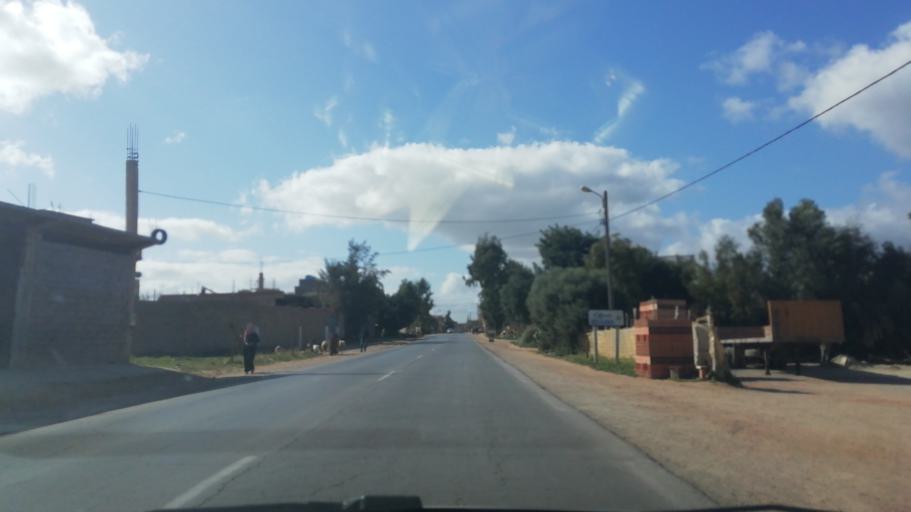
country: DZ
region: Relizane
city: Mazouna
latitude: 36.2764
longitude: 0.6360
